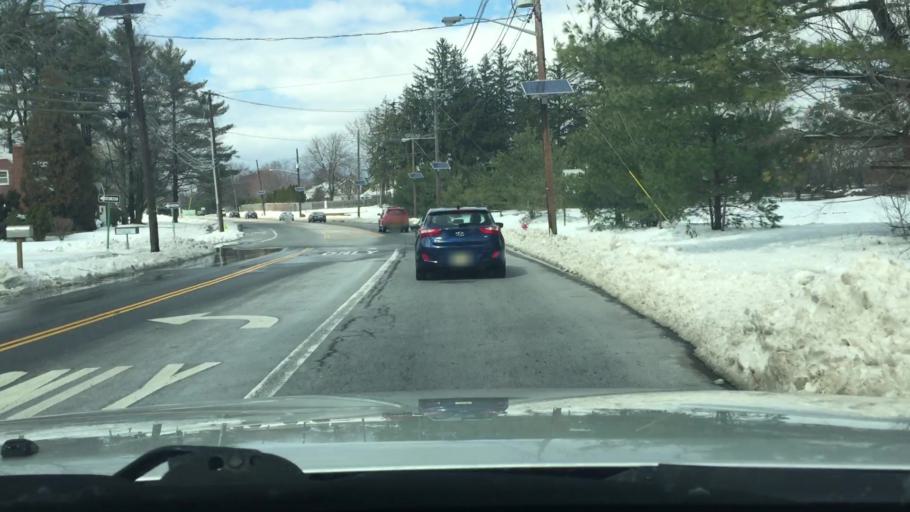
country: US
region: New Jersey
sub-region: Middlesex County
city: East Brunswick
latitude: 40.4280
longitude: -74.4223
